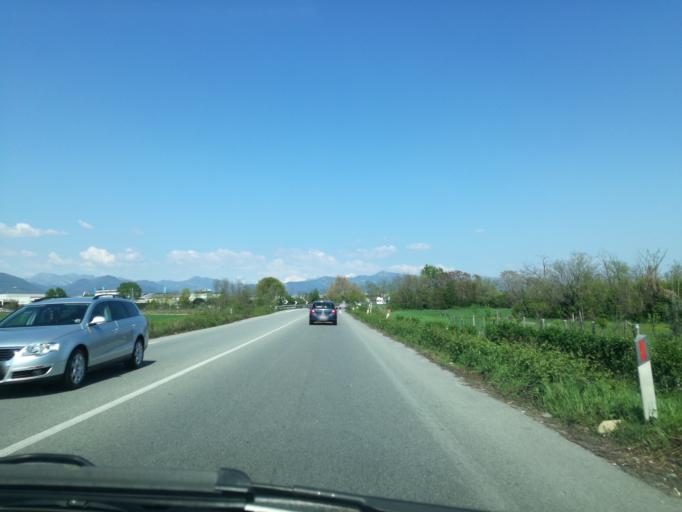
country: IT
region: Lombardy
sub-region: Provincia di Bergamo
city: Bonate Sopra
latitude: 45.6905
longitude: 9.5501
